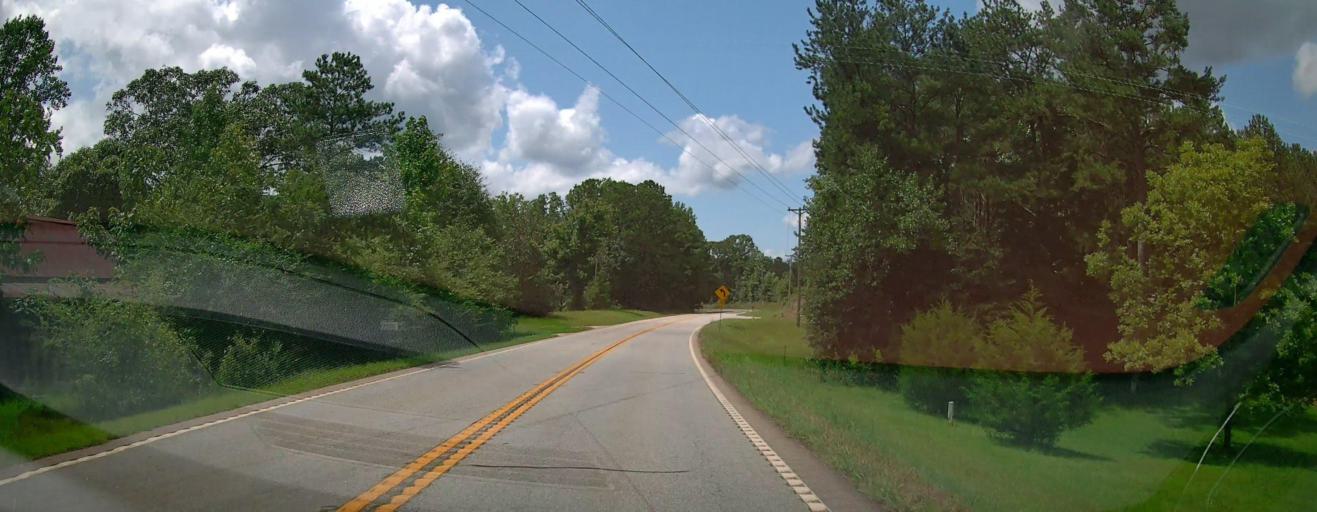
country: US
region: Georgia
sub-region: Heard County
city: Franklin
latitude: 33.3125
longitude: -85.1452
